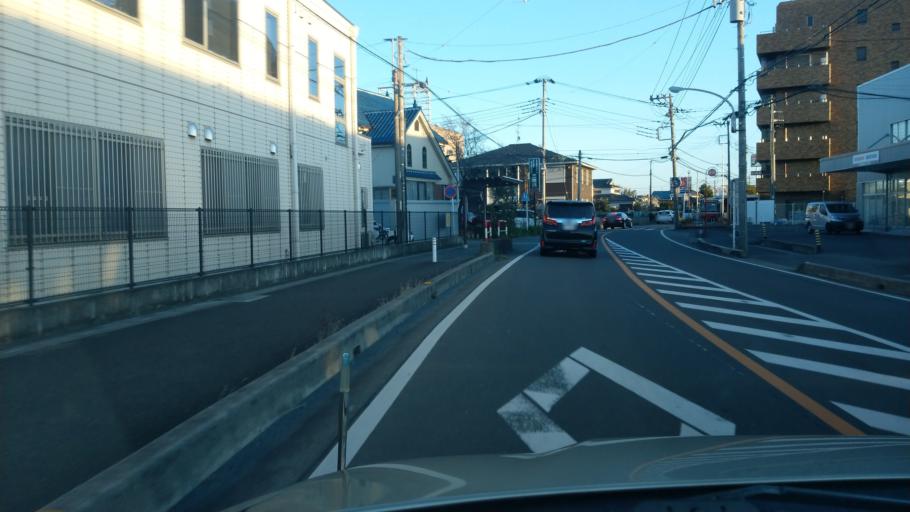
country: JP
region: Saitama
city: Ageoshimo
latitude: 35.9403
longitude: 139.5717
